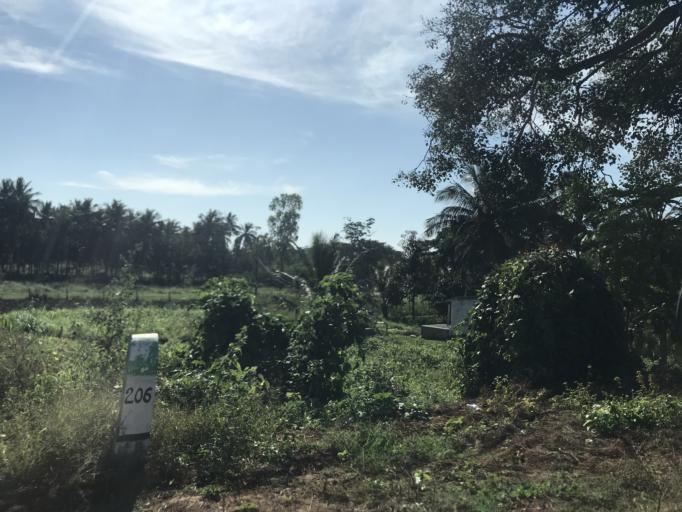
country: IN
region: Karnataka
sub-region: Mysore
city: Mysore
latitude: 12.1951
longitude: 76.5444
